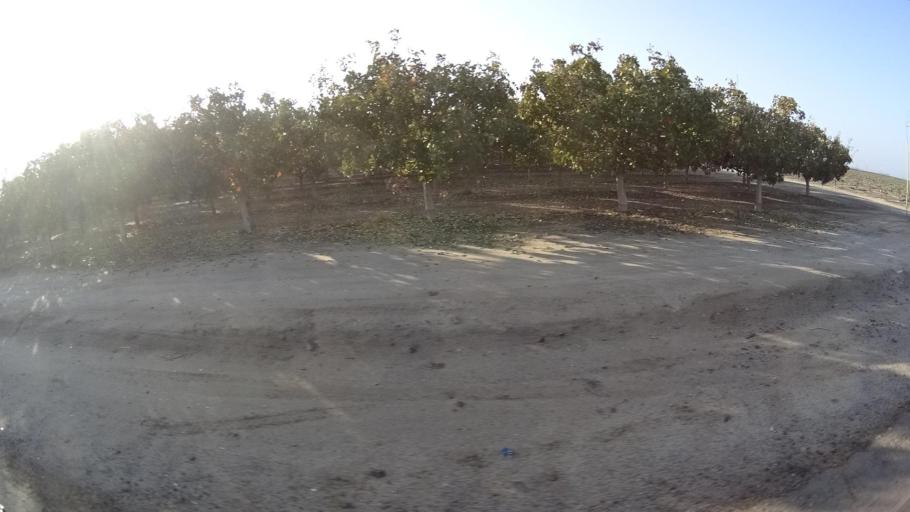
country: US
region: California
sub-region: Tulare County
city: Richgrove
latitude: 35.7906
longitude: -119.1519
